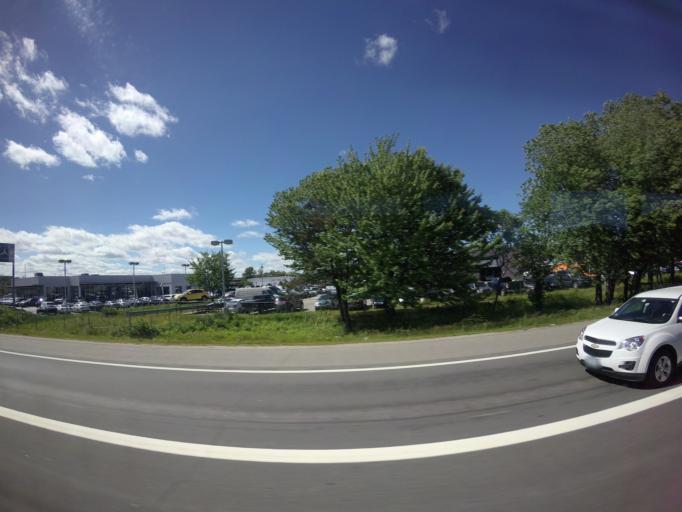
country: US
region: New Hampshire
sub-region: Hillsborough County
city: Manchester
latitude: 42.9559
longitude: -71.4399
